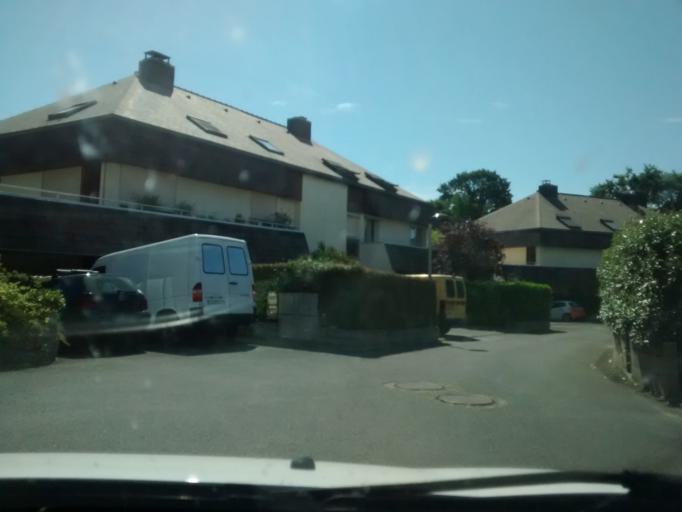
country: FR
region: Brittany
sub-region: Departement d'Ille-et-Vilaine
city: Chantepie
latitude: 48.1135
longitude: -1.6328
